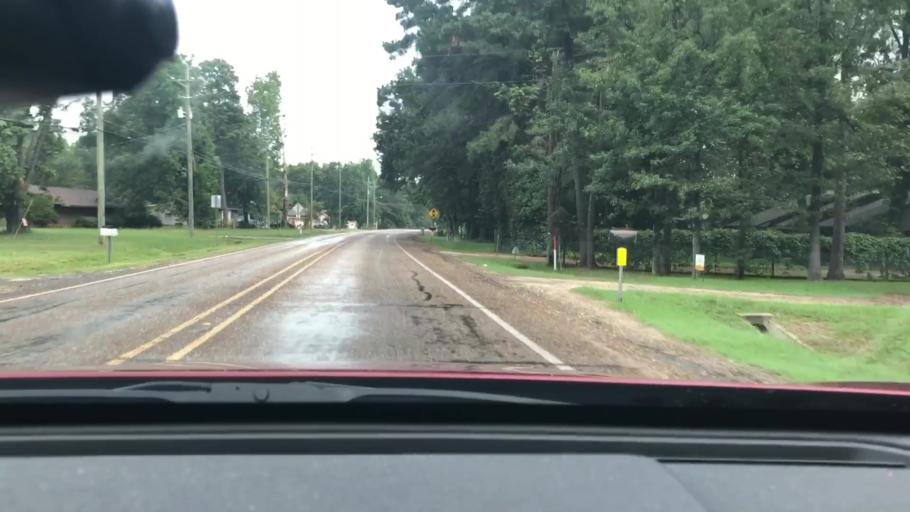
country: US
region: Texas
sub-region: Bowie County
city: Nash
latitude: 33.4422
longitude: -94.1353
